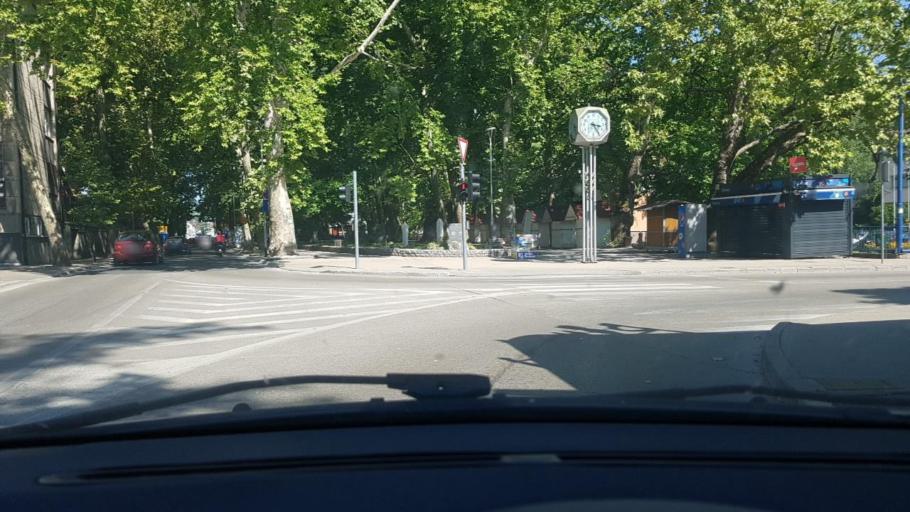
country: BA
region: Federation of Bosnia and Herzegovina
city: Bihac
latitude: 44.8133
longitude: 15.8683
